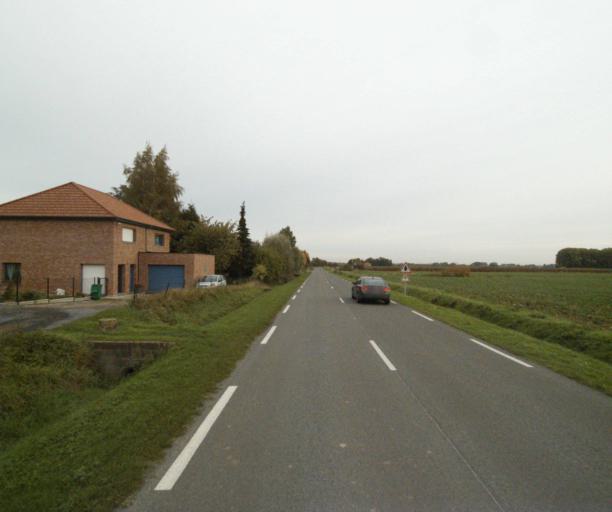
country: FR
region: Nord-Pas-de-Calais
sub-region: Departement du Nord
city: Aubers
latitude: 50.5962
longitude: 2.8315
